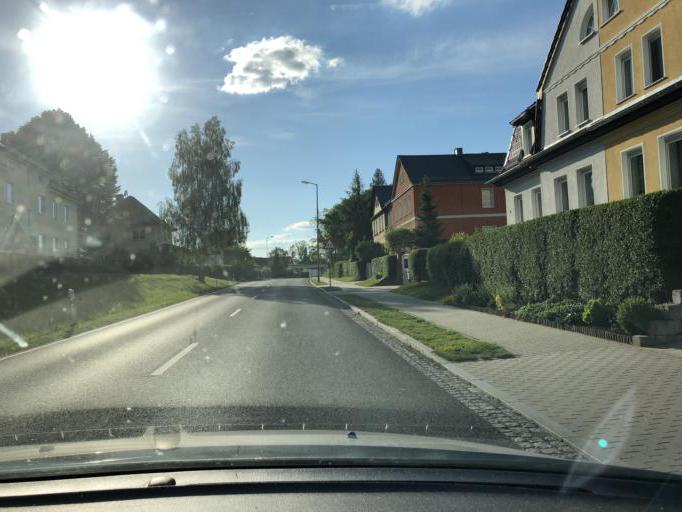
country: DE
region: Thuringia
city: Lodla
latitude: 51.0108
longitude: 12.3805
